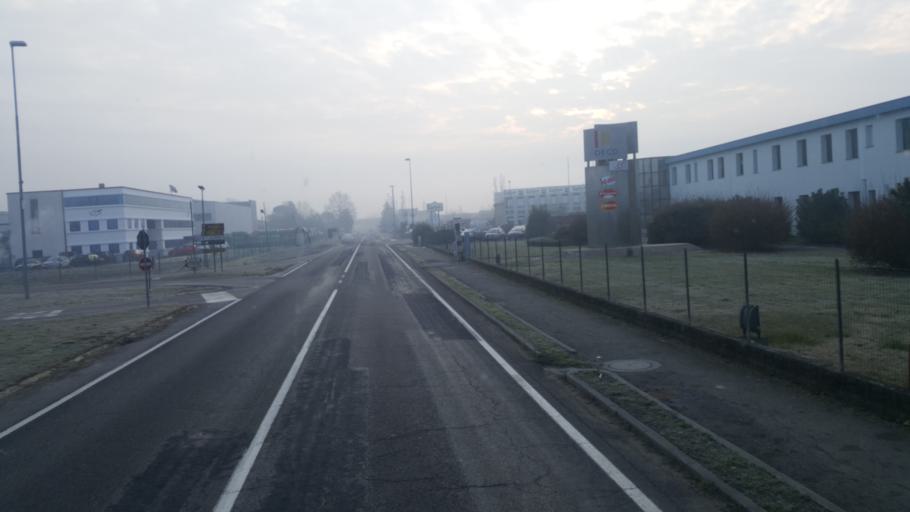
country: IT
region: Emilia-Romagna
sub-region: Provincia di Ravenna
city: Bagnacavallo
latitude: 44.4086
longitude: 11.9973
